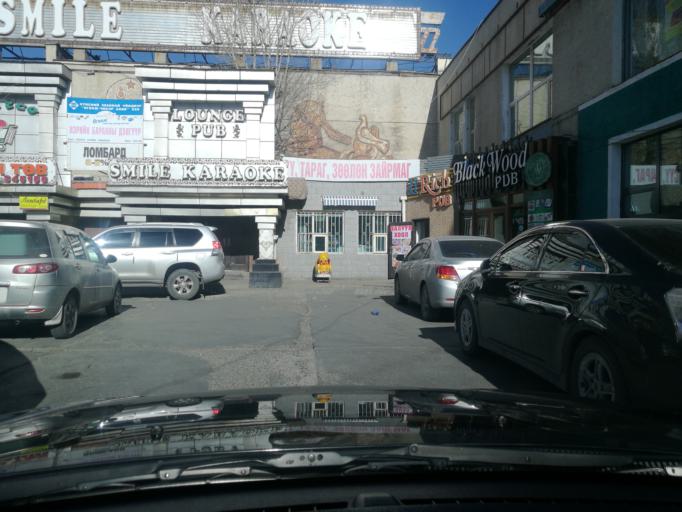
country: MN
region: Ulaanbaatar
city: Ulaanbaatar
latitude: 47.9023
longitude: 106.9017
